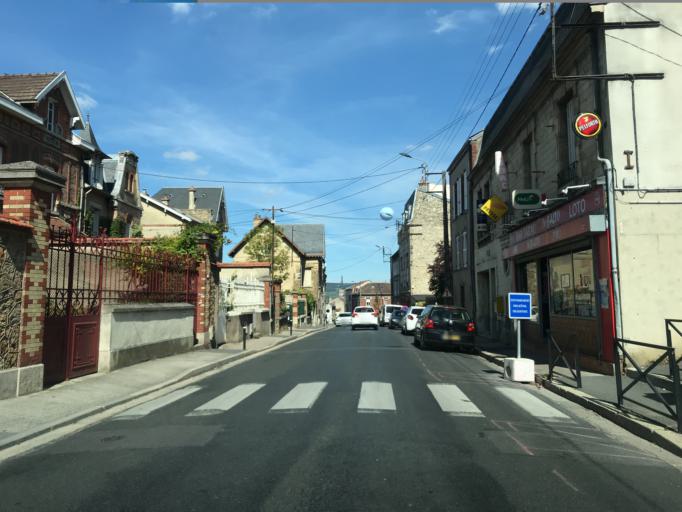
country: FR
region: Champagne-Ardenne
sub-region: Departement de la Marne
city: Epernay
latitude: 49.0342
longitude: 3.9536
